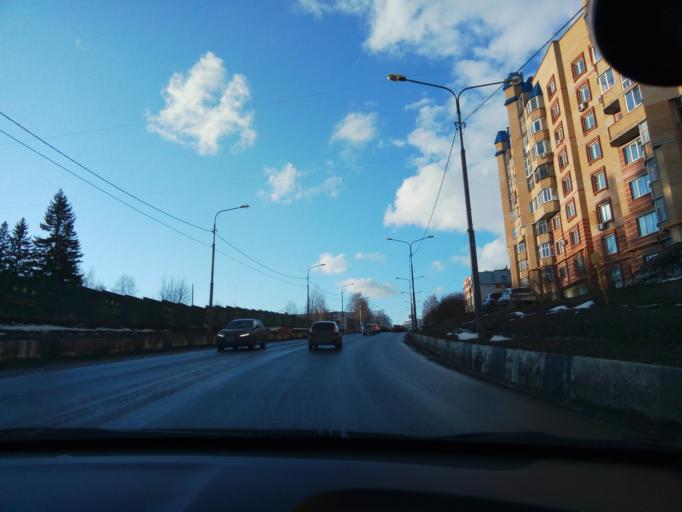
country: RU
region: Chuvashia
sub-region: Cheboksarskiy Rayon
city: Cheboksary
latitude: 56.1401
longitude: 47.2269
